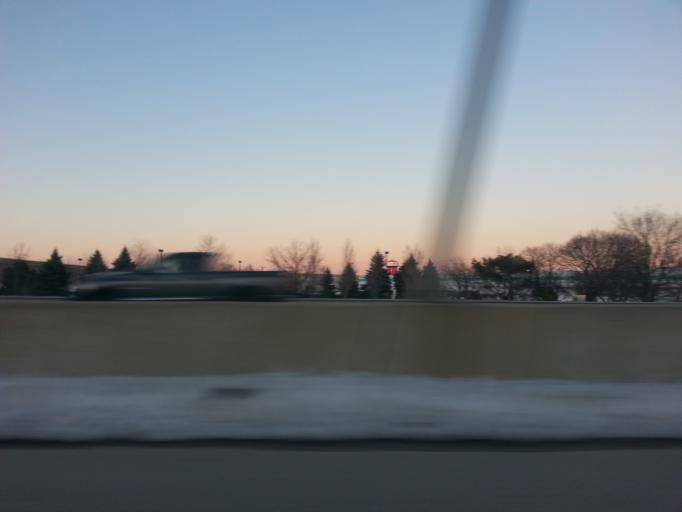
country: US
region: Illinois
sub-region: Cook County
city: Crestwood
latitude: 41.6700
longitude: -87.7599
